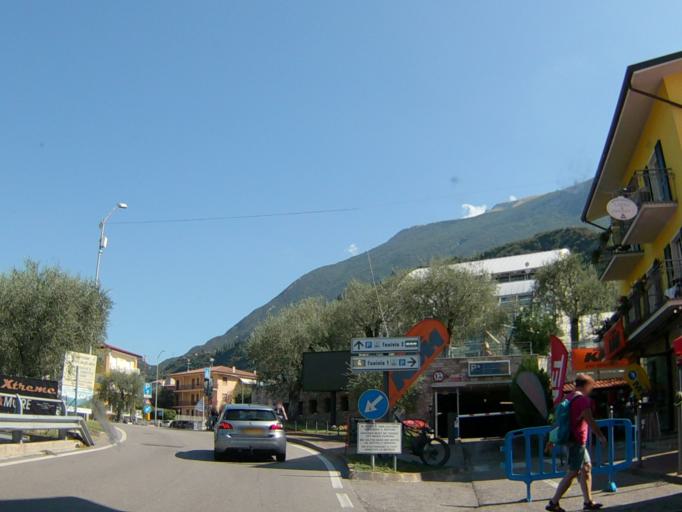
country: IT
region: Veneto
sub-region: Provincia di Verona
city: Malcesine
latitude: 45.7659
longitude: 10.8125
